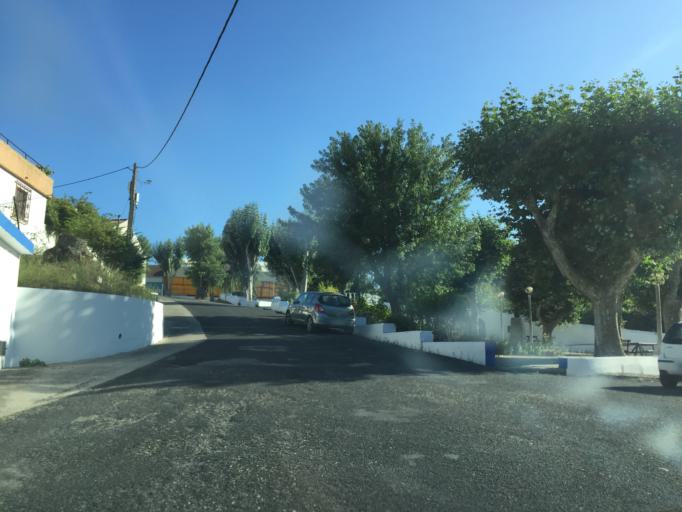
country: PT
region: Lisbon
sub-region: Torres Vedras
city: Torres Vedras
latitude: 39.0907
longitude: -9.2792
